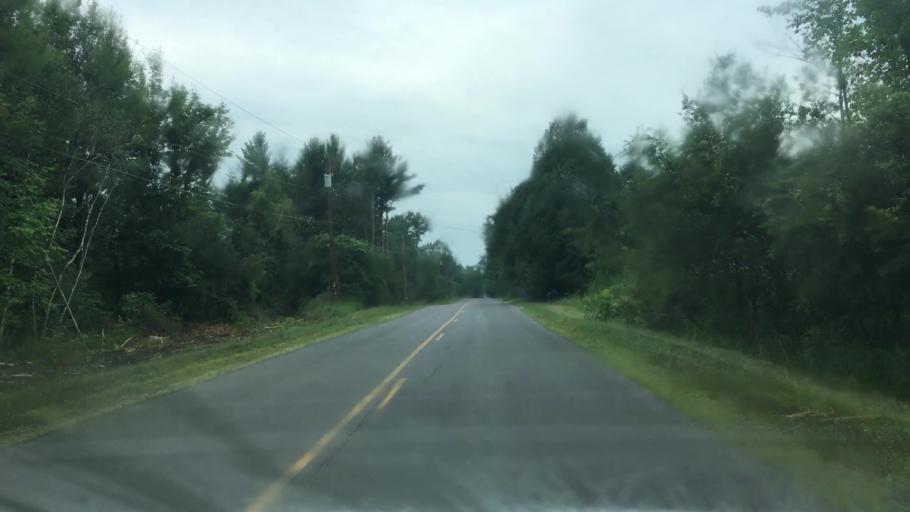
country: US
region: New York
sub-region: Clinton County
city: Morrisonville
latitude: 44.6408
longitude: -73.5836
